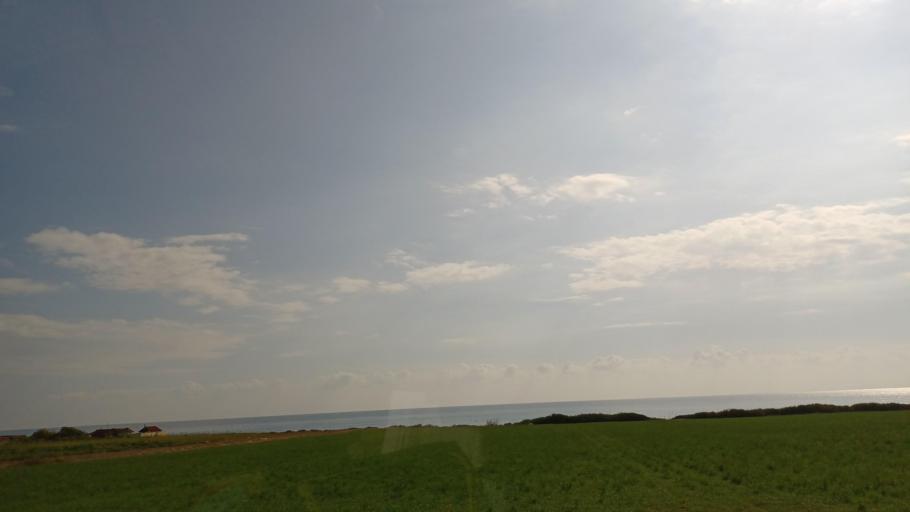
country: CY
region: Larnaka
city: Kofinou
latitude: 34.7750
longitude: 33.4576
